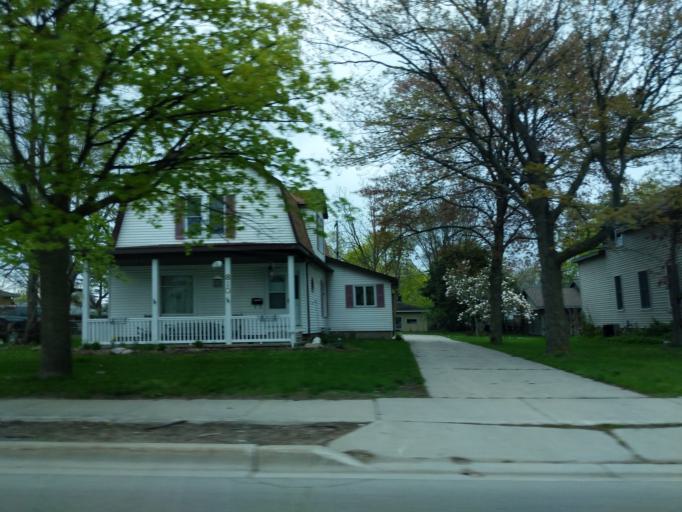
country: US
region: Michigan
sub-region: Tuscola County
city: Vassar
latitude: 43.3731
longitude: -83.5915
